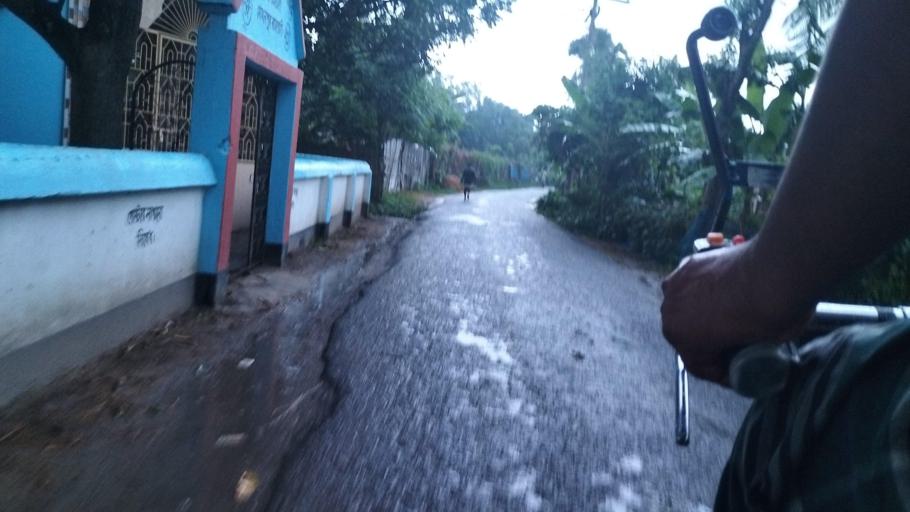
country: BD
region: Rajshahi
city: Rajshahi
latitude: 24.5447
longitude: 88.6308
